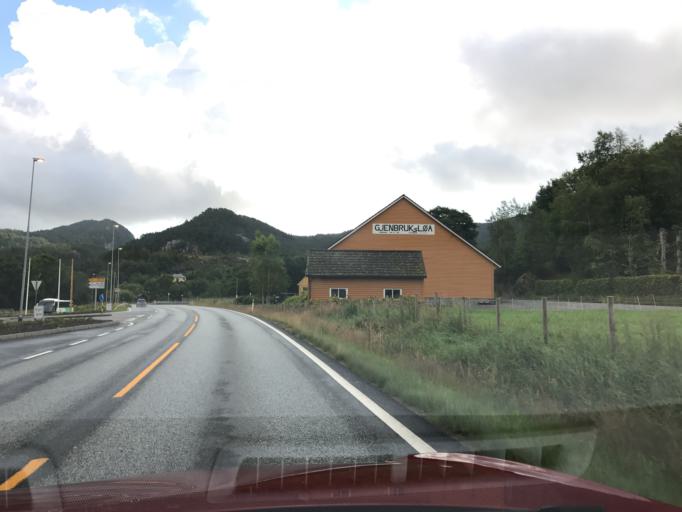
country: NO
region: Hordaland
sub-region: Bomlo
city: Mosterhamn
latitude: 59.6089
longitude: 5.4749
